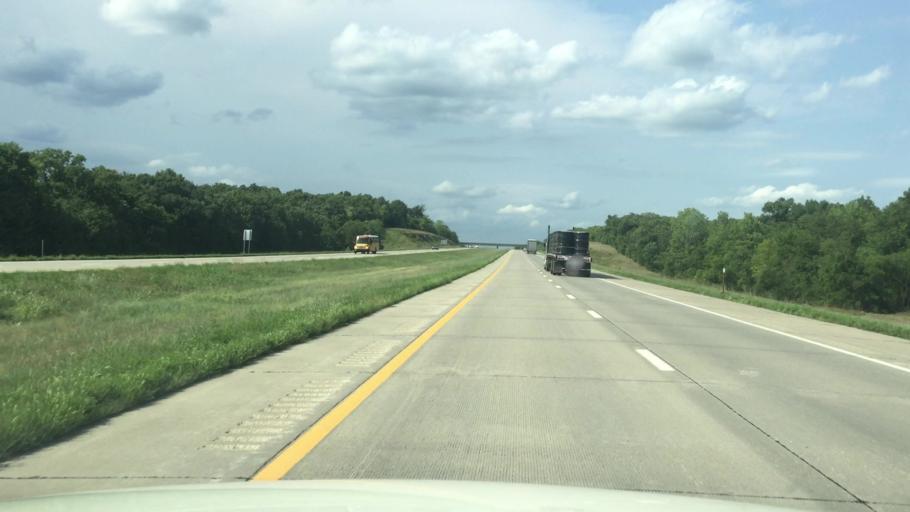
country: US
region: Kansas
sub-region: Miami County
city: Louisburg
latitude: 38.5981
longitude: -94.6940
